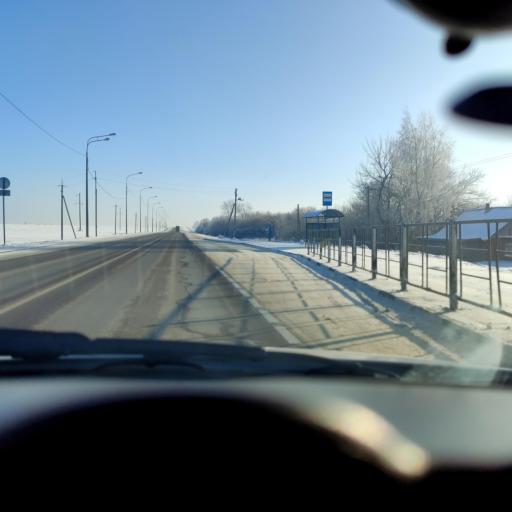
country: RU
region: Kursk
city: Tim
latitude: 51.6554
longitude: 36.9185
